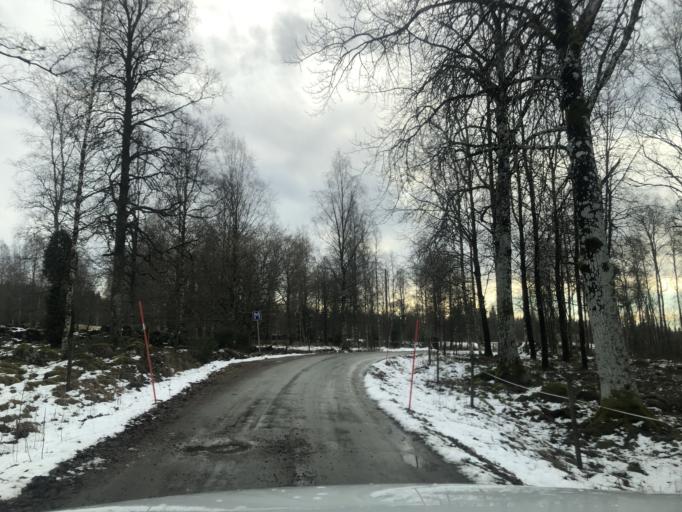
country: SE
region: Vaestra Goetaland
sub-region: Ulricehamns Kommun
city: Ulricehamn
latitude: 57.7723
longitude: 13.4702
